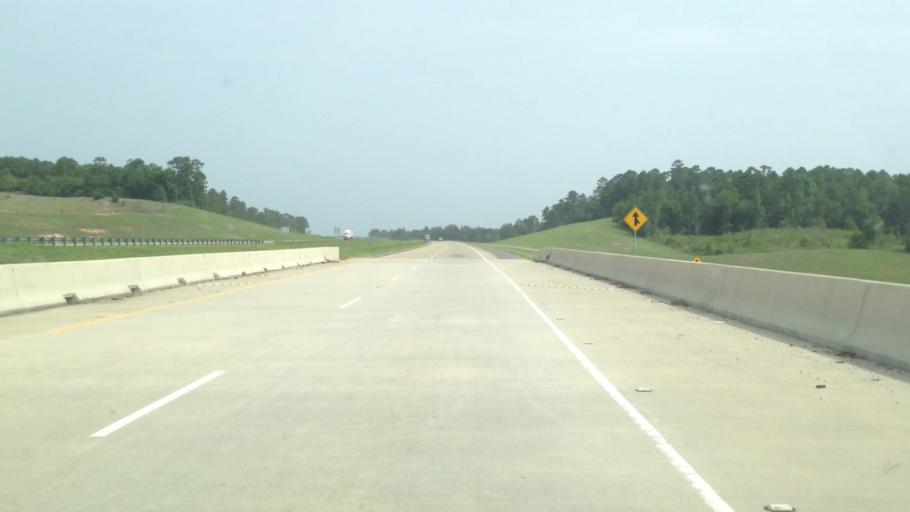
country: US
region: Louisiana
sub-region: Caddo Parish
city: Vivian
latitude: 32.9437
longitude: -93.8976
